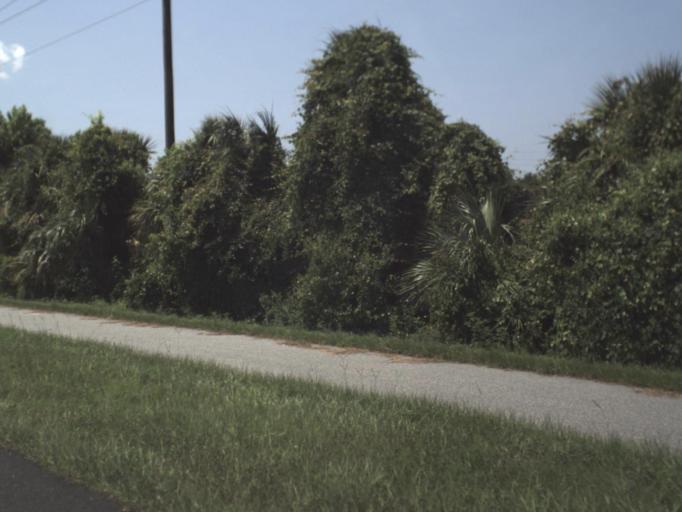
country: US
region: Florida
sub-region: Citrus County
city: Crystal River
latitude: 28.9176
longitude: -82.6096
